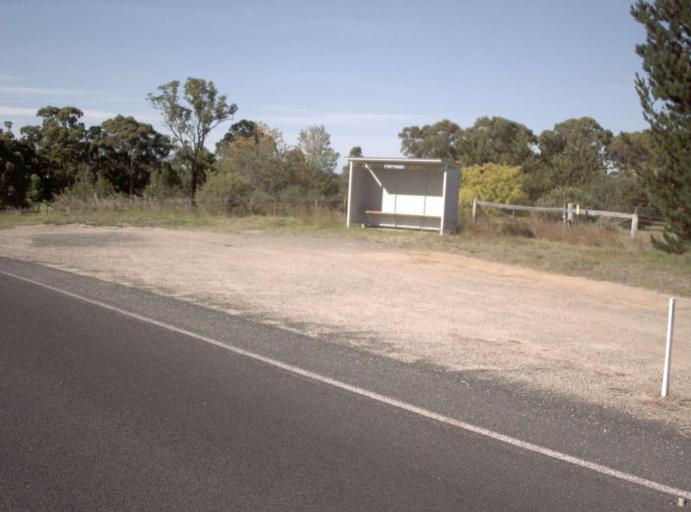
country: AU
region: Victoria
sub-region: East Gippsland
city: Lakes Entrance
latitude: -37.8729
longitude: 147.8478
